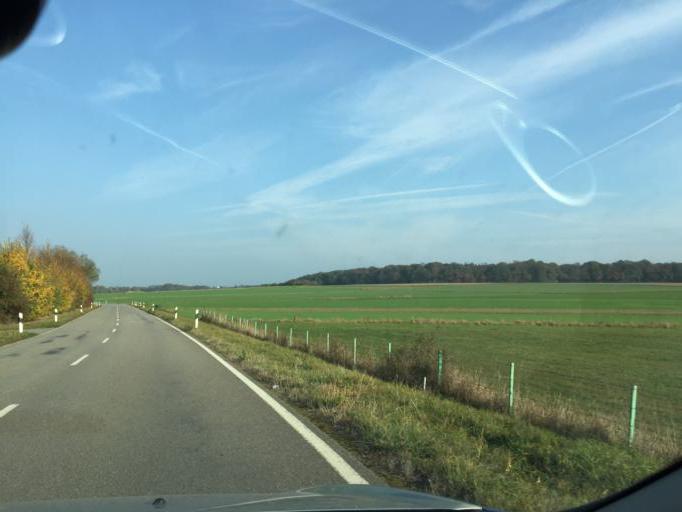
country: LU
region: Luxembourg
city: Aspelt
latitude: 49.5509
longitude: 6.2308
